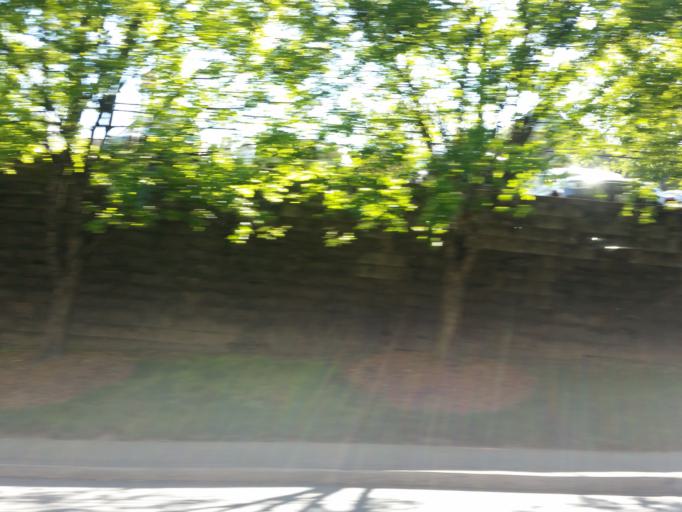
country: US
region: North Carolina
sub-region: Buncombe County
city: Asheville
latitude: 35.5726
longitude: -82.5454
